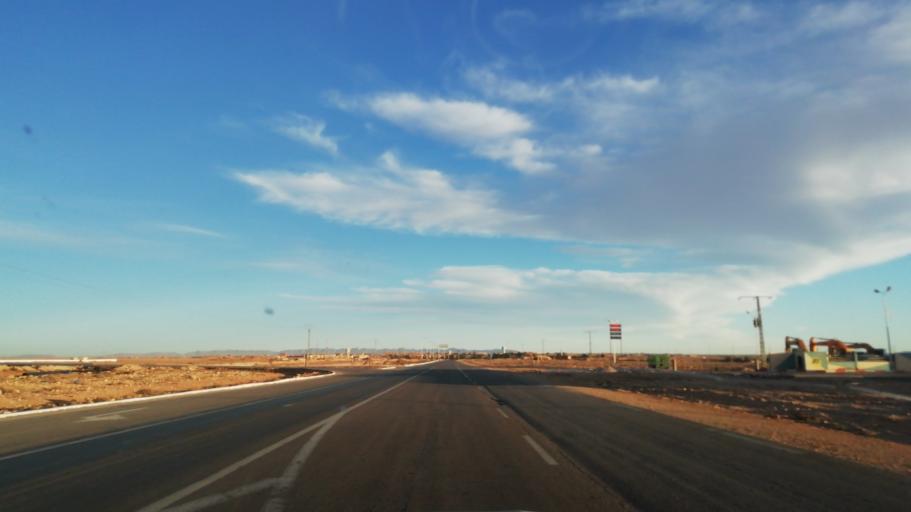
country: DZ
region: Wilaya de Naama
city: Naama
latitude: 33.7262
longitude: -0.7439
